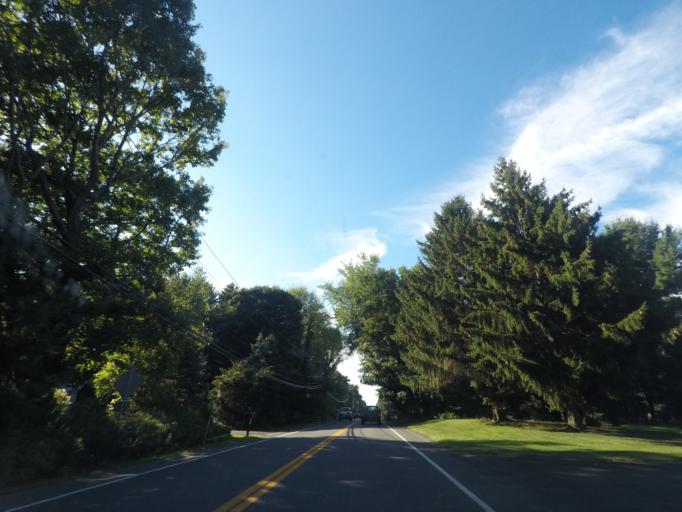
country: US
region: New York
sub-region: Albany County
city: West Albany
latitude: 42.7080
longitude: -73.7577
